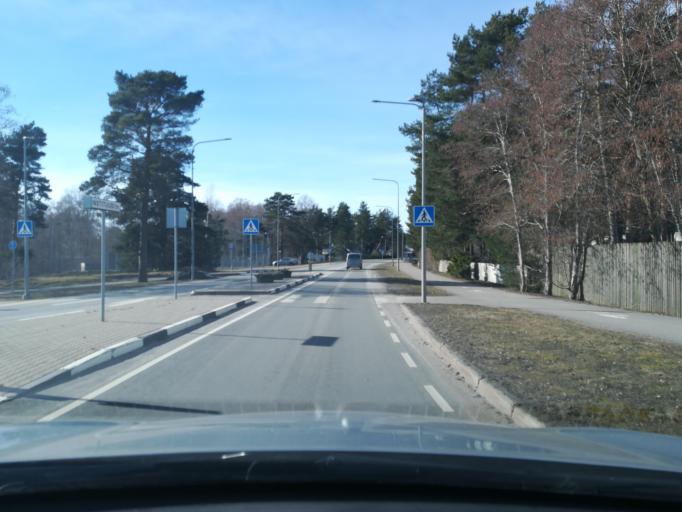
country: EE
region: Harju
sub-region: Saue vald
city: Laagri
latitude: 59.3533
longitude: 24.6084
